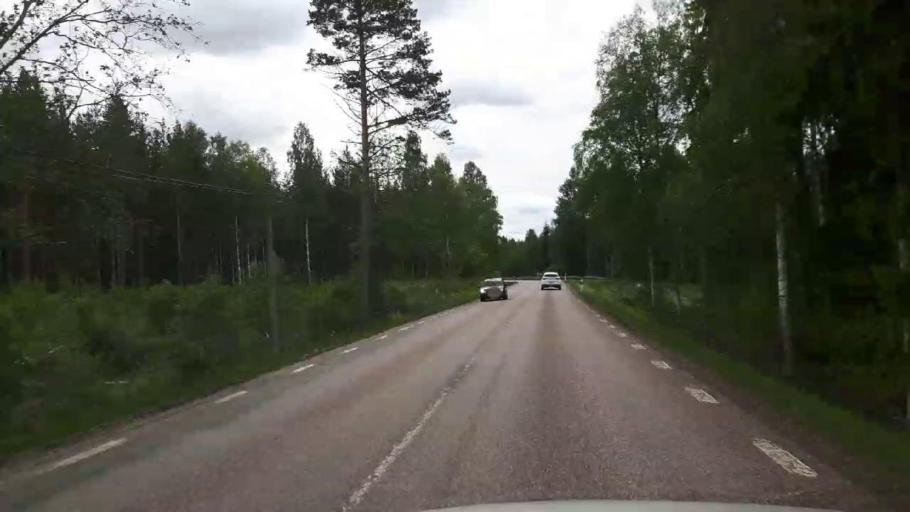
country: SE
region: Vaestmanland
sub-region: Norbergs Kommun
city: Norberg
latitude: 60.1144
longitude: 15.9193
